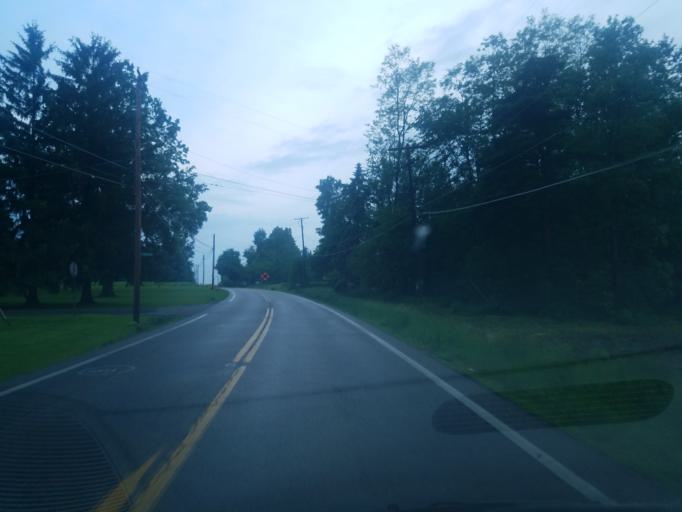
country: US
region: Ohio
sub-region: Columbiana County
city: Salem
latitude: 40.8780
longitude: -80.8817
